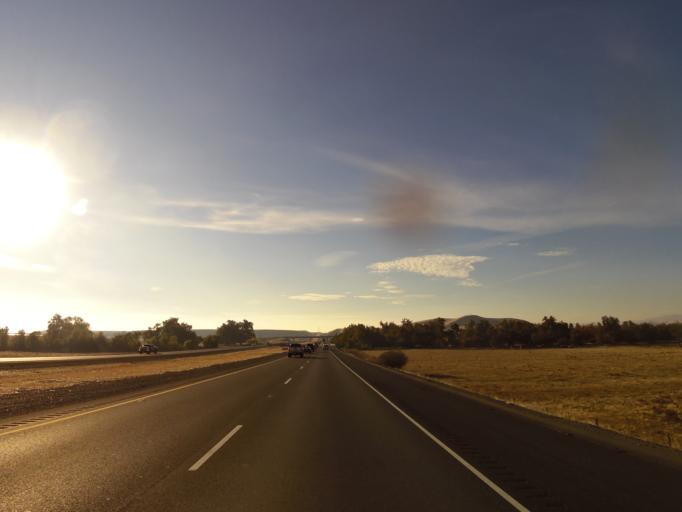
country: US
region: California
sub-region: Stanislaus County
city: Newman
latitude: 37.3316
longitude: -121.1123
